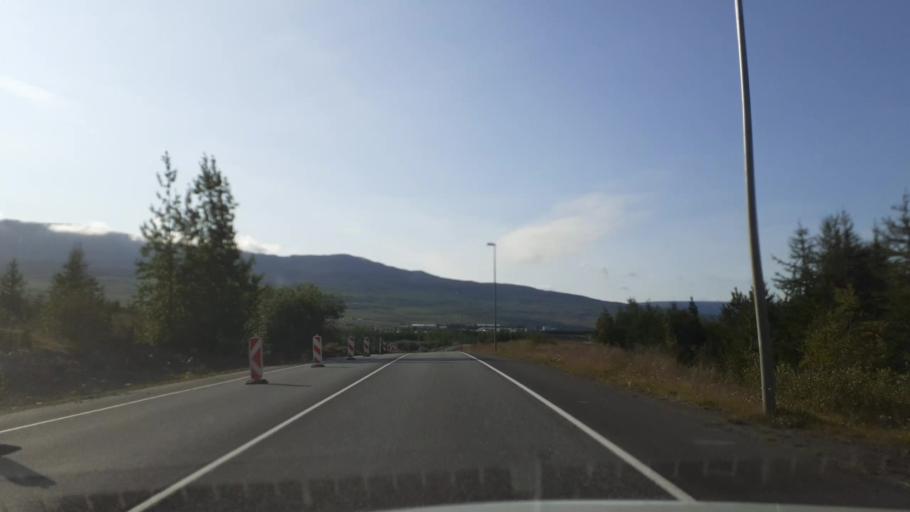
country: IS
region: Northeast
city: Akureyri
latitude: 65.6707
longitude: -18.1130
